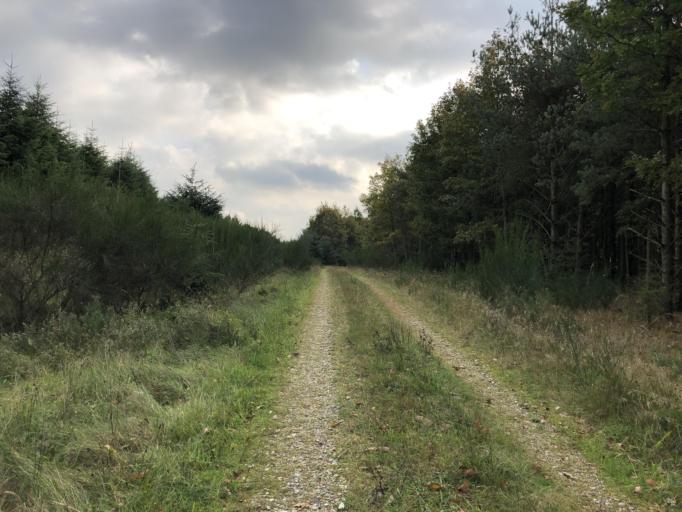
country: DK
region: Central Jutland
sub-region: Holstebro Kommune
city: Ulfborg
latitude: 56.2197
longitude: 8.4358
